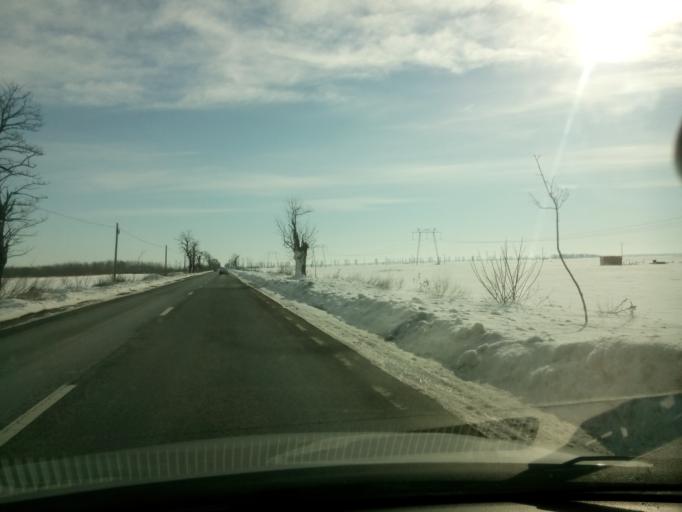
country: RO
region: Calarasi
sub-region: Comuna Frumusani
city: Frumusani
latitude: 44.2613
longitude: 26.3562
